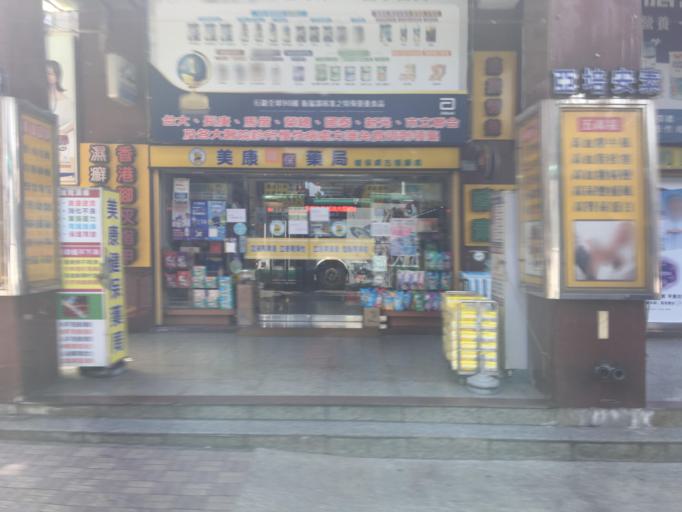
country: TW
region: Taipei
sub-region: Taipei
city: Banqiao
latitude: 25.0453
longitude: 121.4257
